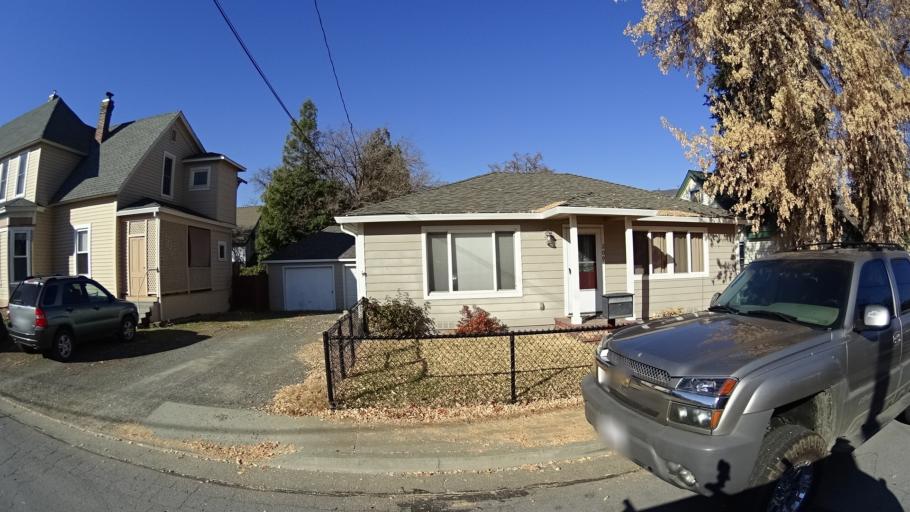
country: US
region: California
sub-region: Siskiyou County
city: Yreka
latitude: 41.7335
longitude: -122.6393
